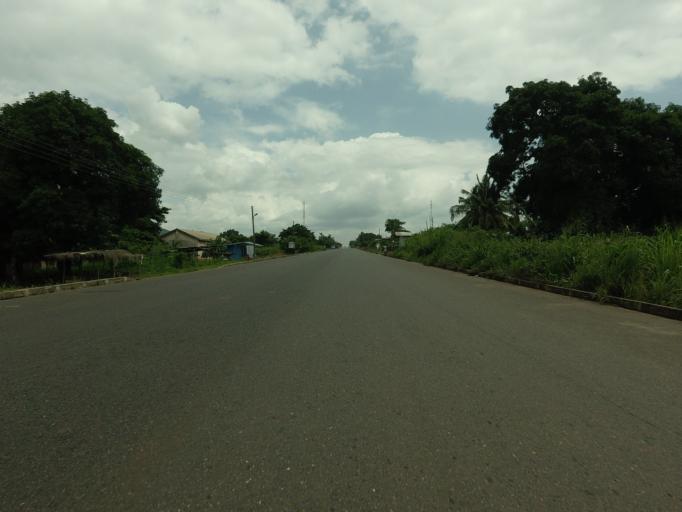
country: GH
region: Volta
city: Ho
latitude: 6.5357
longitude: 0.2314
